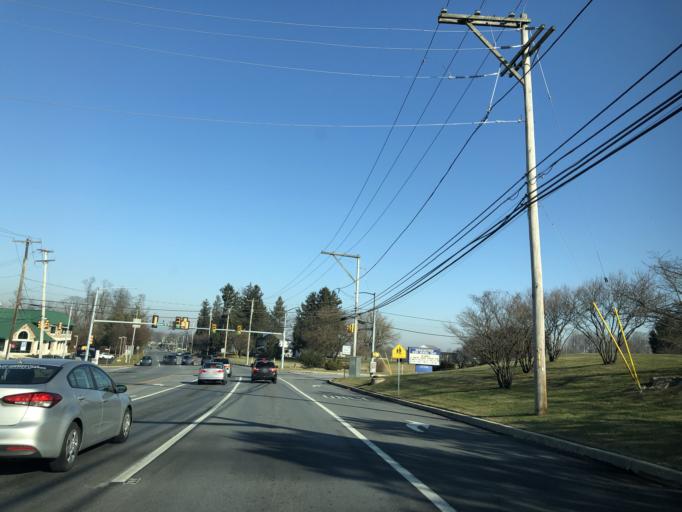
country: US
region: Pennsylvania
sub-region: Chester County
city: Exton
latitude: 40.0438
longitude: -75.6634
